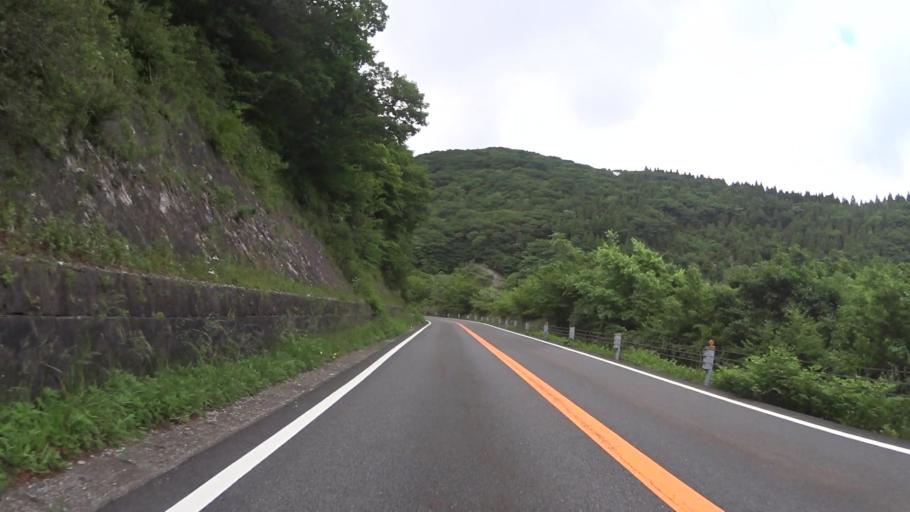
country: JP
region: Kumamoto
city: Aso
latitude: 33.0858
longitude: 131.1937
